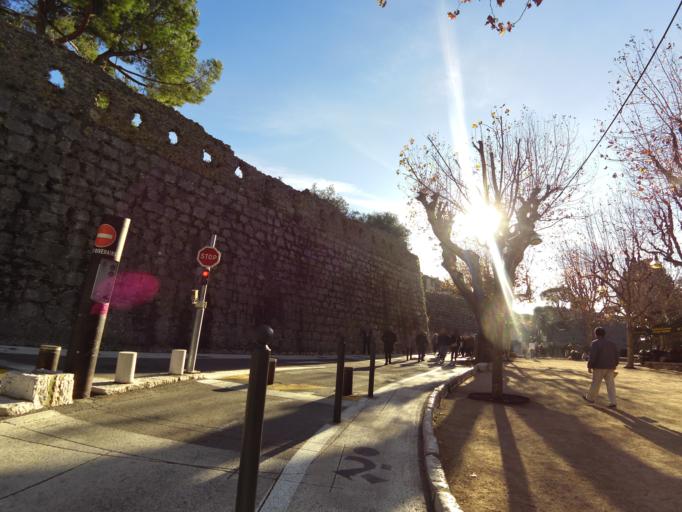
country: FR
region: Provence-Alpes-Cote d'Azur
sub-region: Departement des Alpes-Maritimes
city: Saint-Paul-de-Vence
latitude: 43.6992
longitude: 7.1215
